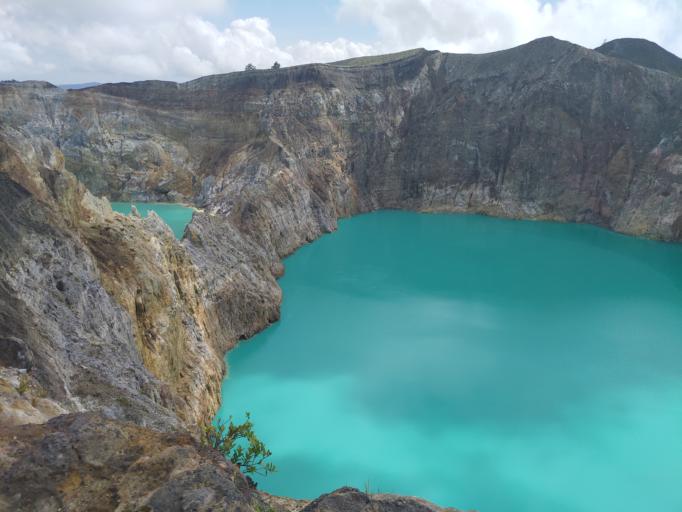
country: ID
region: East Nusa Tenggara
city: Koanara
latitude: -8.7691
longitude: 121.8149
